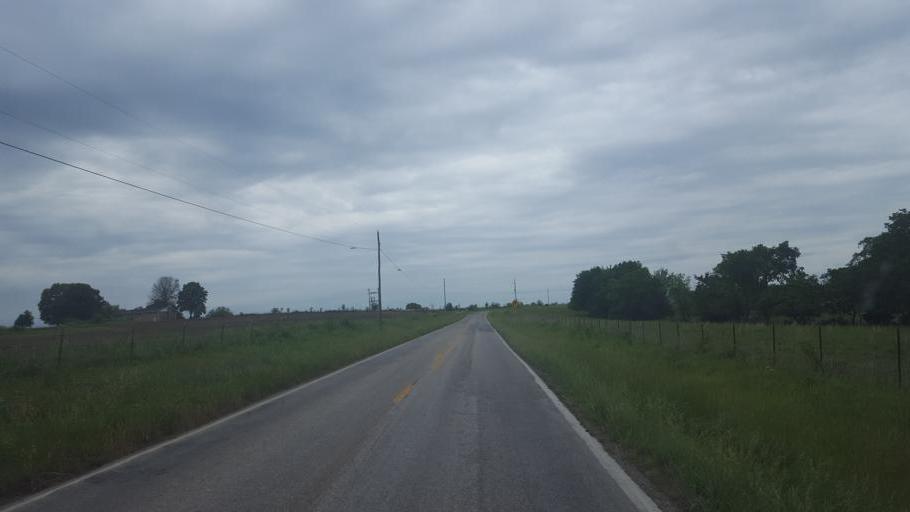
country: US
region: Missouri
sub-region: Moniteau County
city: California
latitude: 38.6697
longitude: -92.5856
